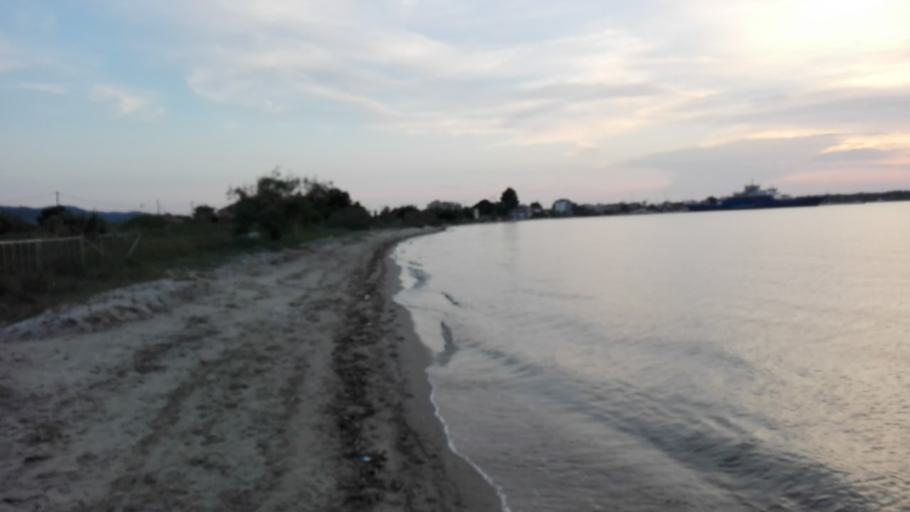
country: GR
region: East Macedonia and Thrace
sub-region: Nomos Kavalas
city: Prinos
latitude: 40.7603
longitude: 24.5846
